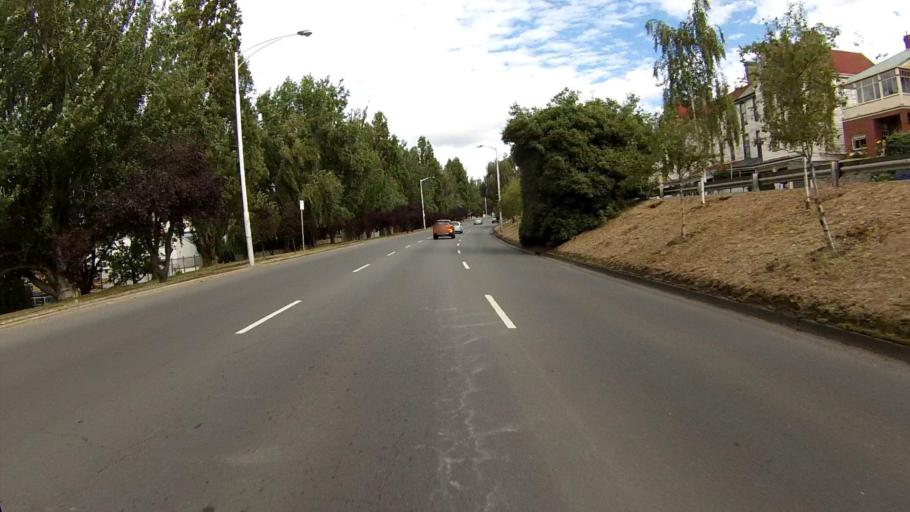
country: AU
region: Tasmania
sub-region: Hobart
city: Hobart
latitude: -42.8759
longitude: 147.3270
